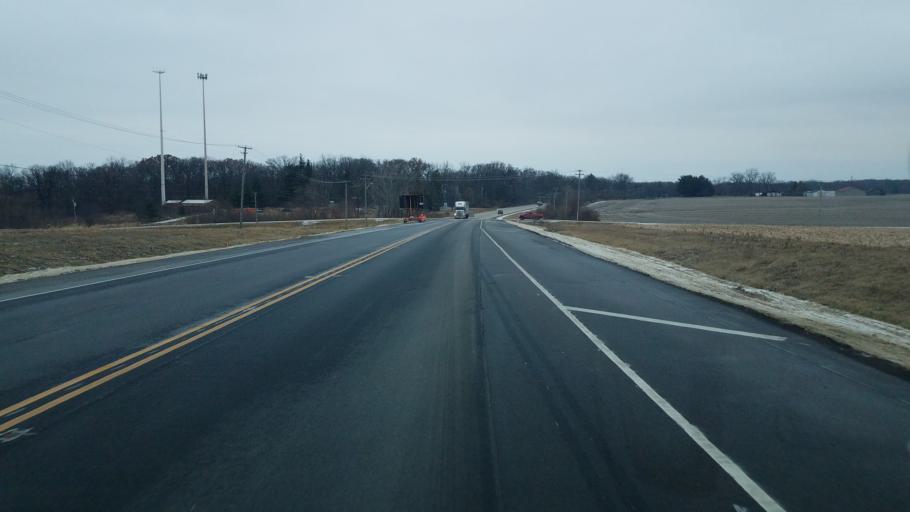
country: US
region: Illinois
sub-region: Kane County
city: Sugar Grove
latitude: 41.8216
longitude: -88.4673
